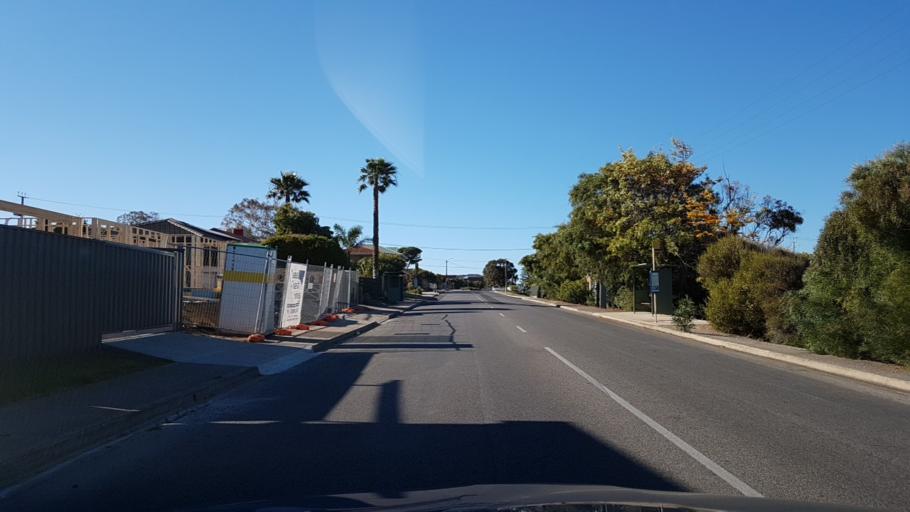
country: AU
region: South Australia
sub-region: Adelaide
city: Port Noarlunga
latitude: -35.1333
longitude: 138.4733
